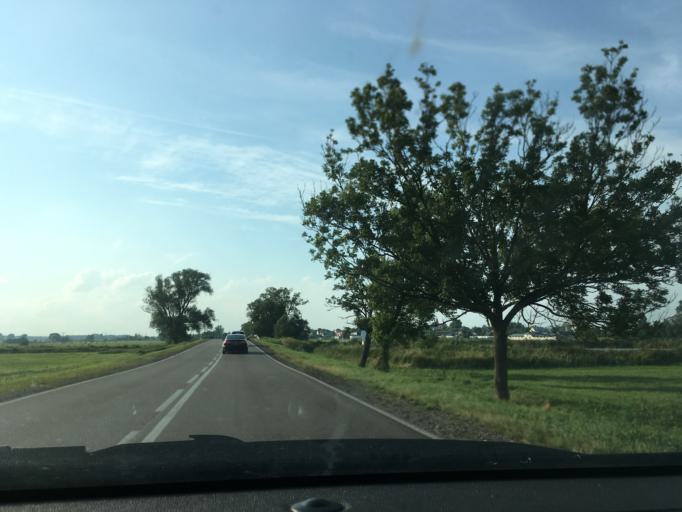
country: PL
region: Podlasie
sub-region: Powiat moniecki
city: Knyszyn
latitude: 53.3018
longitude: 22.9230
